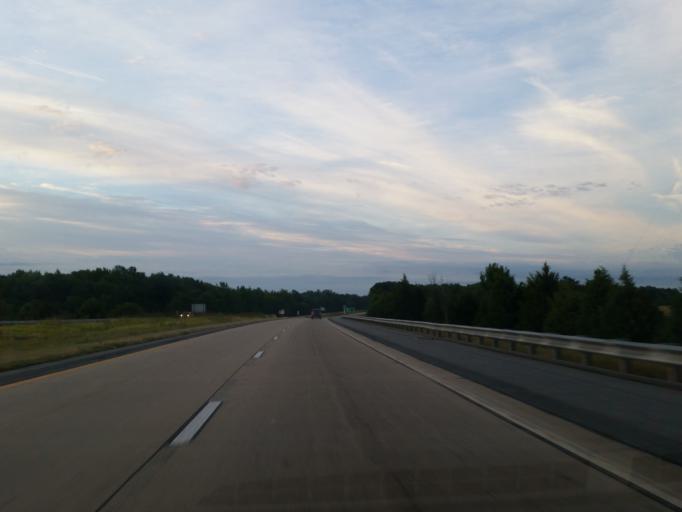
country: US
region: Delaware
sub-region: Kent County
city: Smyrna
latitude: 39.2718
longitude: -75.5823
